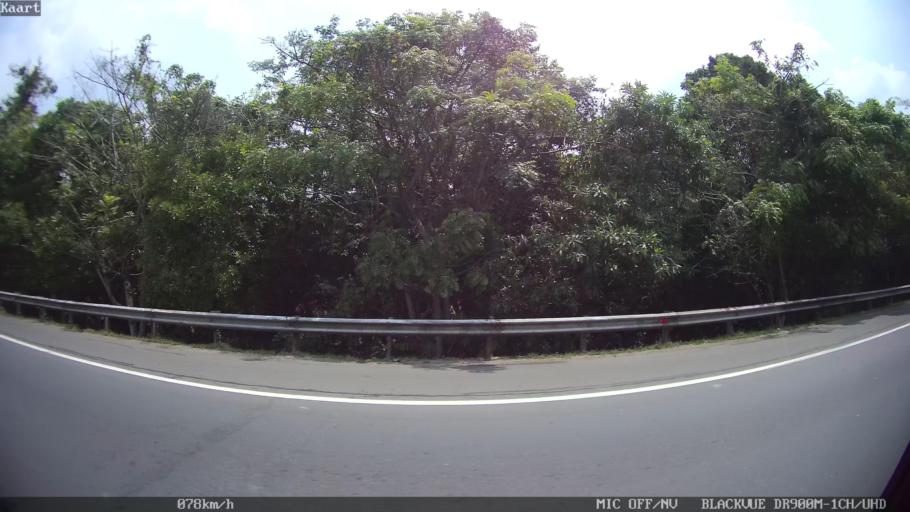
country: ID
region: Banten
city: Serang
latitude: -6.0766
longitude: 106.1312
